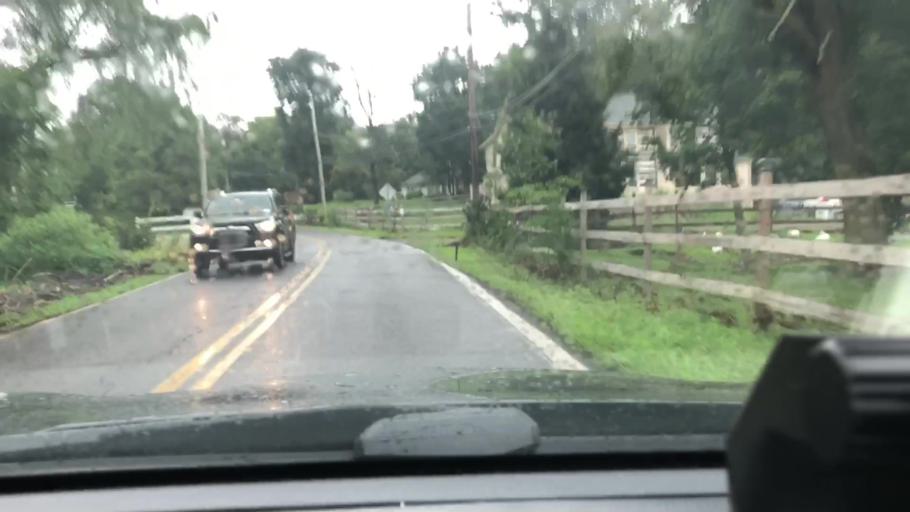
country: US
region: Pennsylvania
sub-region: Bucks County
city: Spinnerstown
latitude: 40.4685
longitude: -75.4225
